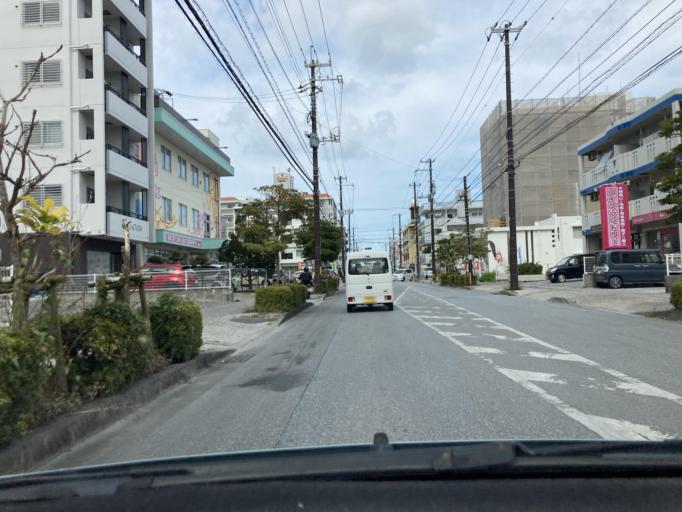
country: JP
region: Okinawa
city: Naha-shi
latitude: 26.2342
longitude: 127.6913
